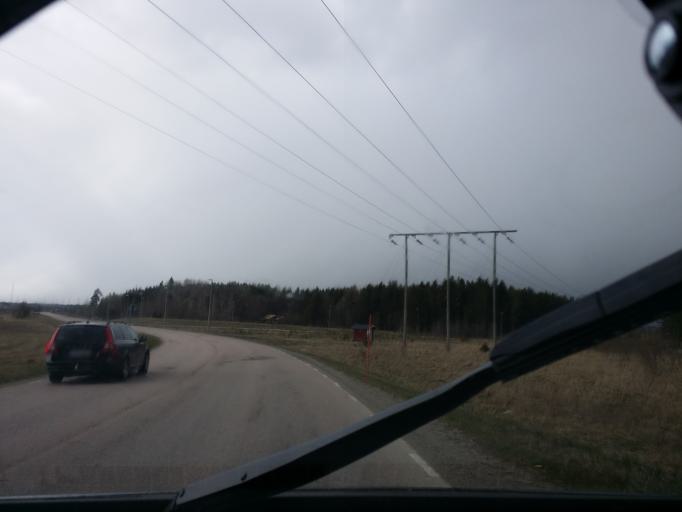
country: SE
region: Uppsala
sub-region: Enkopings Kommun
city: Enkoping
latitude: 59.6424
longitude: 17.1451
